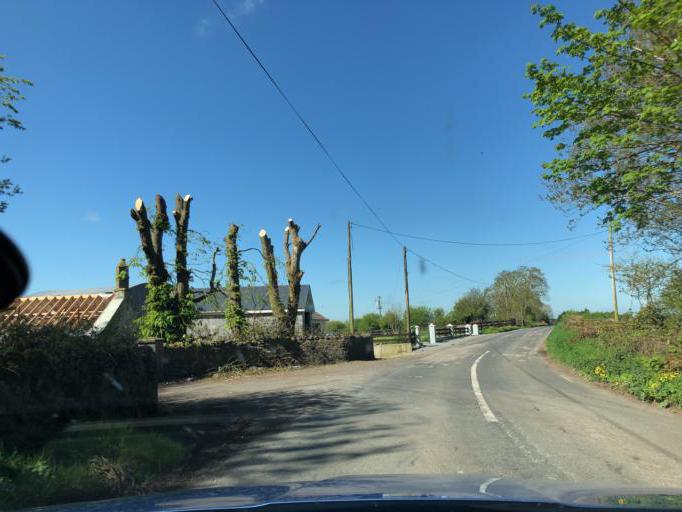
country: IE
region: Leinster
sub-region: Uibh Fhaili
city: Banagher
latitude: 53.2005
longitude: -8.0507
